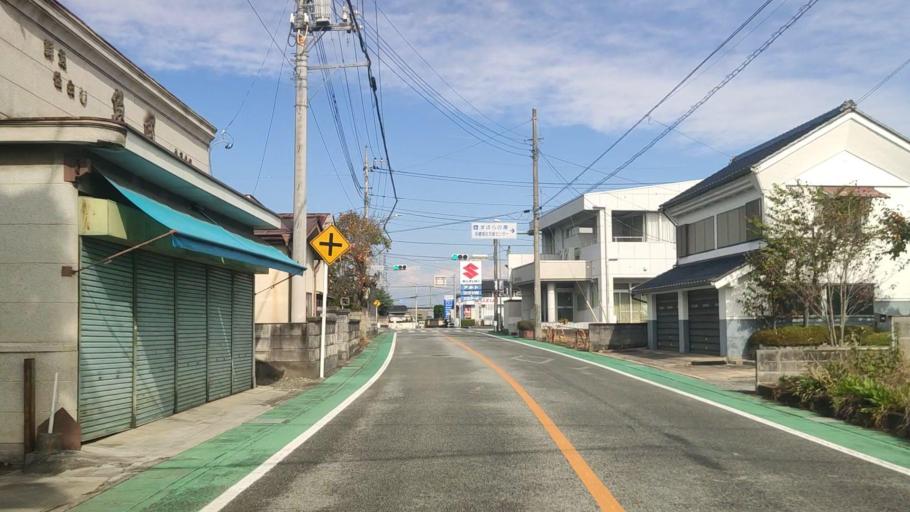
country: JP
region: Yamanashi
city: Ryuo
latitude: 35.5725
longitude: 138.4648
